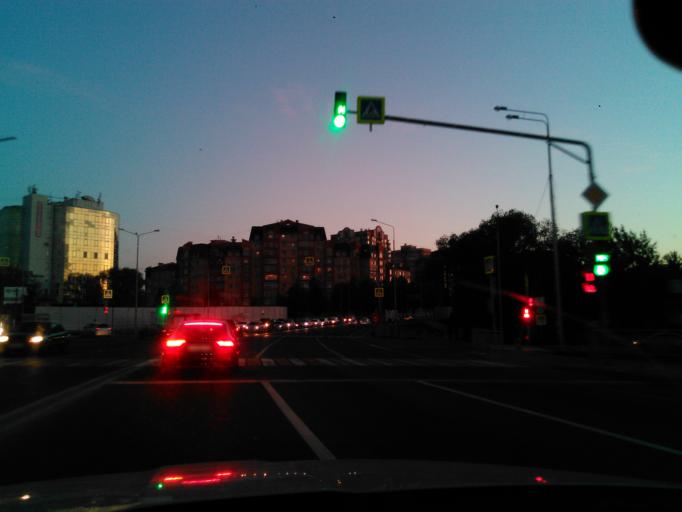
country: RU
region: Moskovskaya
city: Dolgoprudnyy
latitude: 55.9487
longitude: 37.5072
